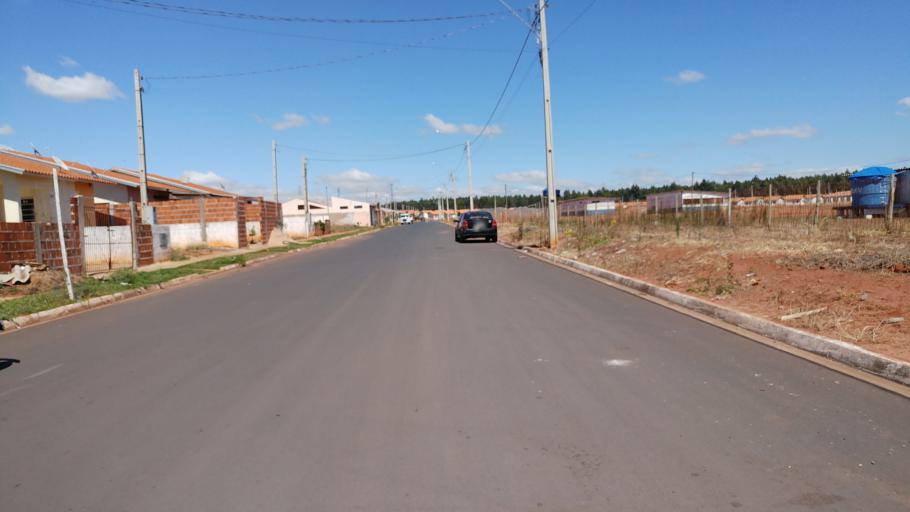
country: BR
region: Sao Paulo
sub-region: Paraguacu Paulista
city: Paraguacu Paulista
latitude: -22.4445
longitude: -50.5843
